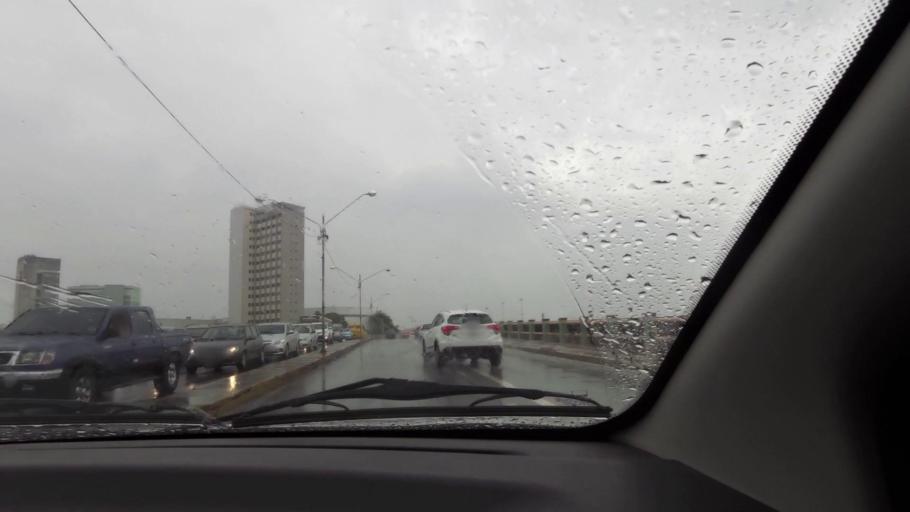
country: BR
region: Pernambuco
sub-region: Recife
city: Recife
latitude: -8.0680
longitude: -34.8744
